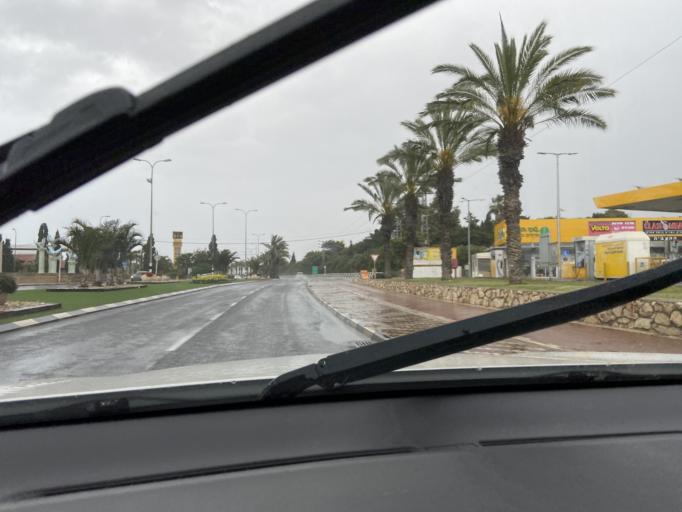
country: IL
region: Northern District
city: El Mazra`a
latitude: 32.9901
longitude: 35.0960
